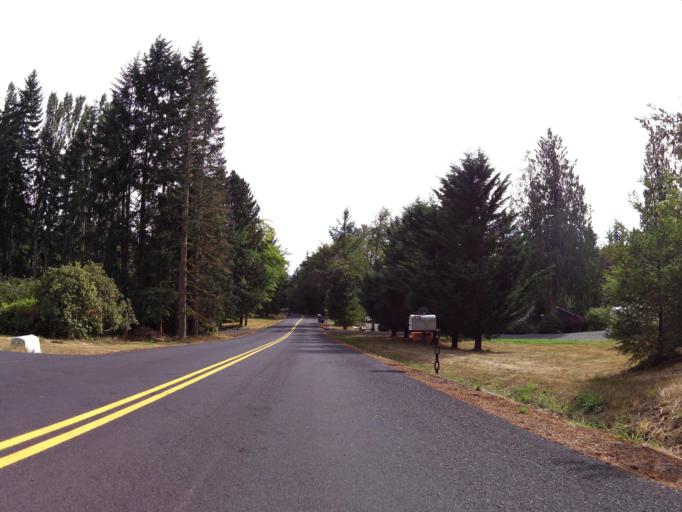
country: US
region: Washington
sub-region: Cowlitz County
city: Castle Rock
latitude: 46.3112
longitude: -122.9239
